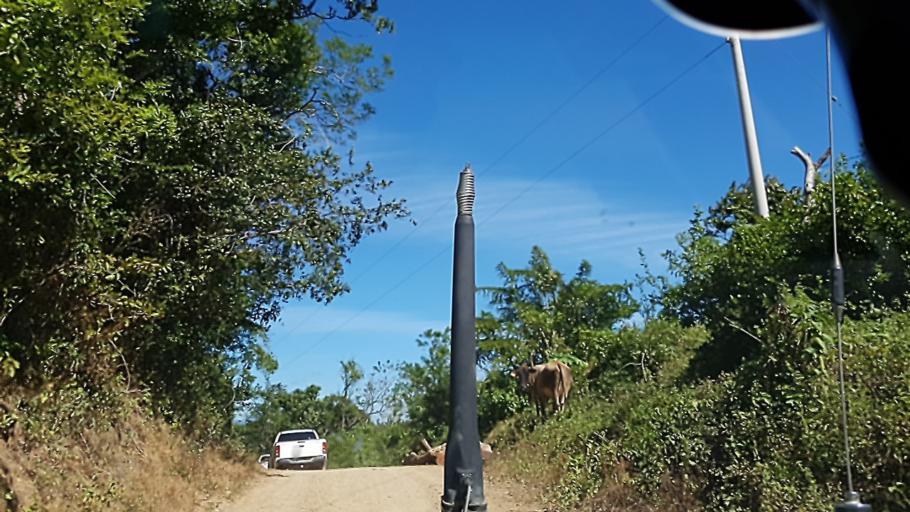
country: NI
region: Carazo
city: Santa Teresa
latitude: 11.6691
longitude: -86.1762
